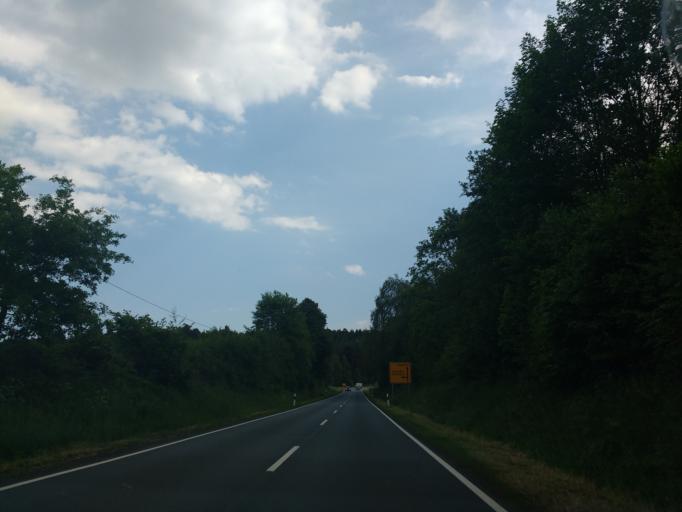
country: DE
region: Hesse
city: Frankenberg
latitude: 51.0259
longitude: 8.8240
